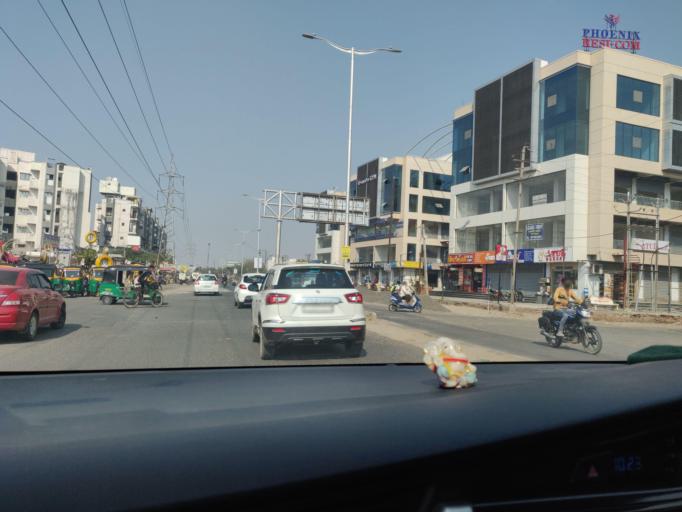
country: IN
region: Gujarat
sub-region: Vadodara
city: Vadodara
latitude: 22.2978
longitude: 73.2497
